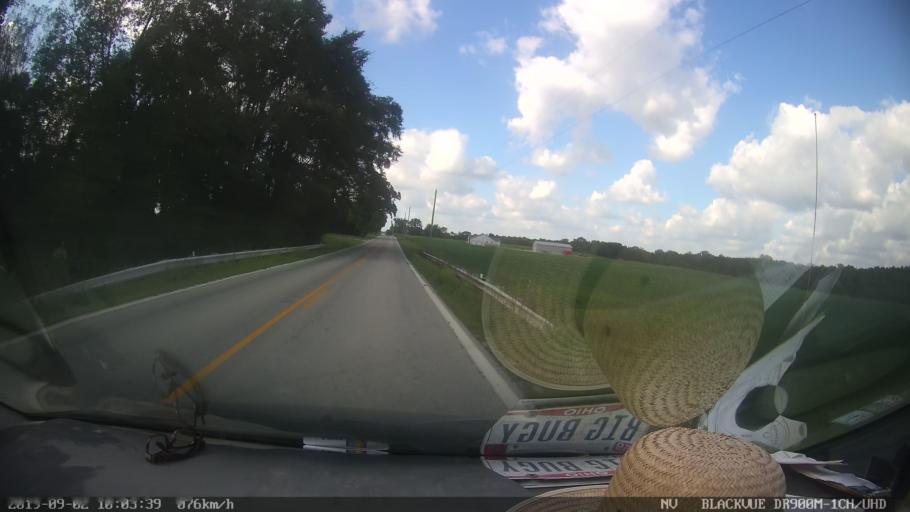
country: US
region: Ohio
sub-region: Delaware County
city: Ashley
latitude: 40.4772
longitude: -82.9722
